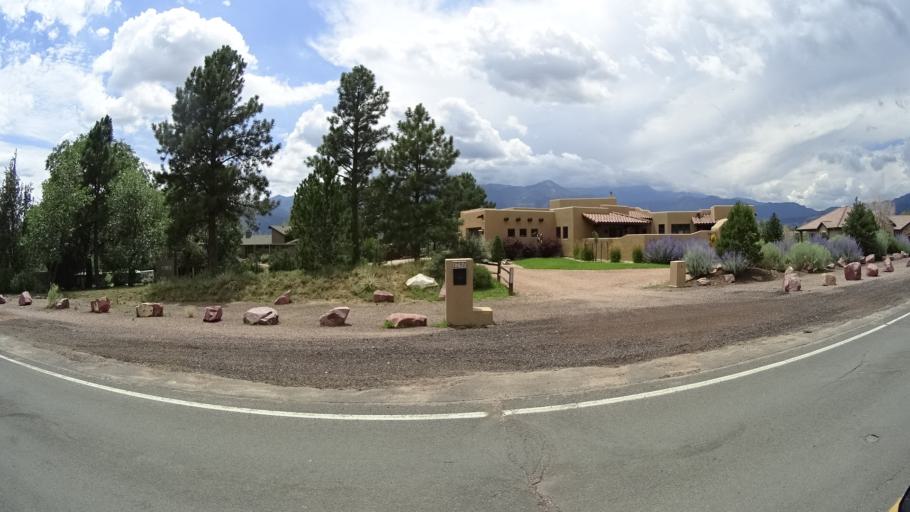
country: US
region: Colorado
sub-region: El Paso County
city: Colorado Springs
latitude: 38.8575
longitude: -104.8466
